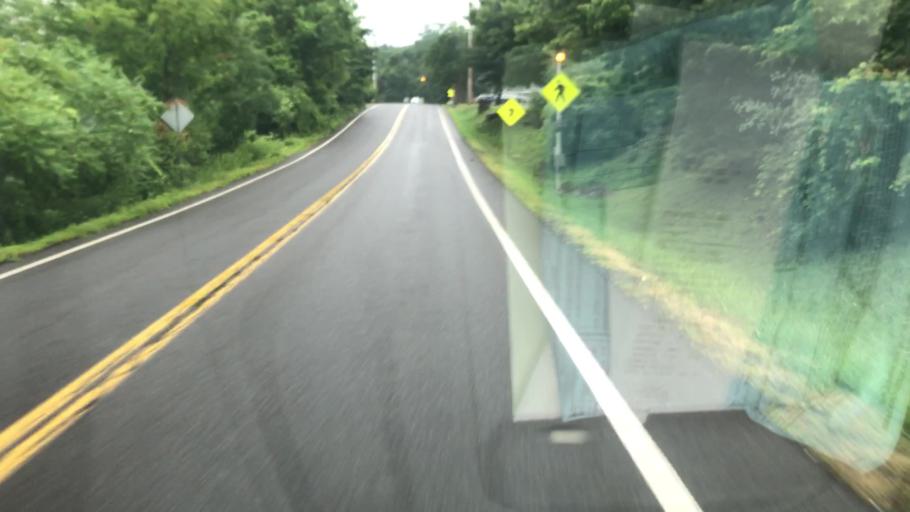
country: US
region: New York
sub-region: Onondaga County
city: Manlius
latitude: 43.0036
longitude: -76.0025
